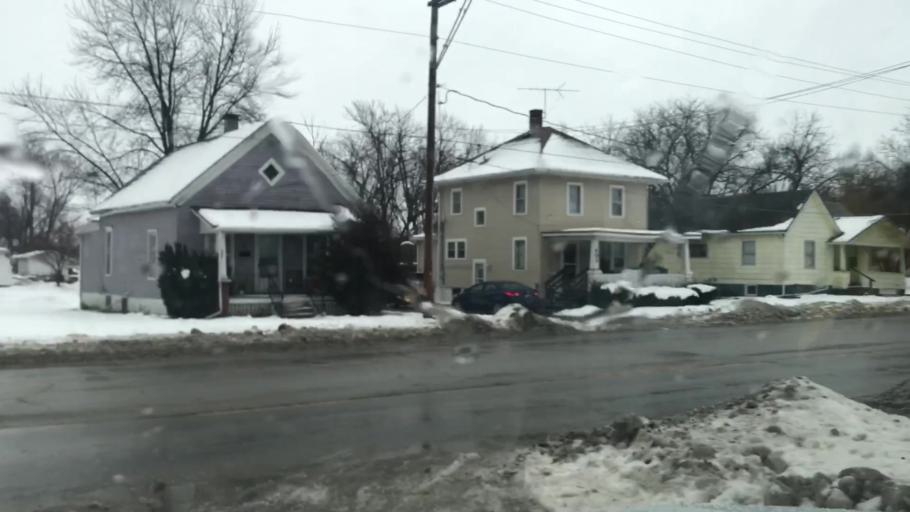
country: US
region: Missouri
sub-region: Clinton County
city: Cameron
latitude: 39.7370
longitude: -94.2361
